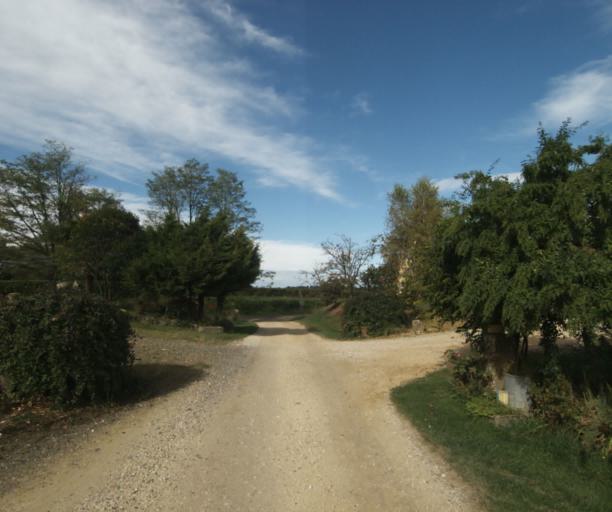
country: FR
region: Midi-Pyrenees
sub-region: Departement du Gers
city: Cazaubon
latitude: 43.9030
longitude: -0.1493
